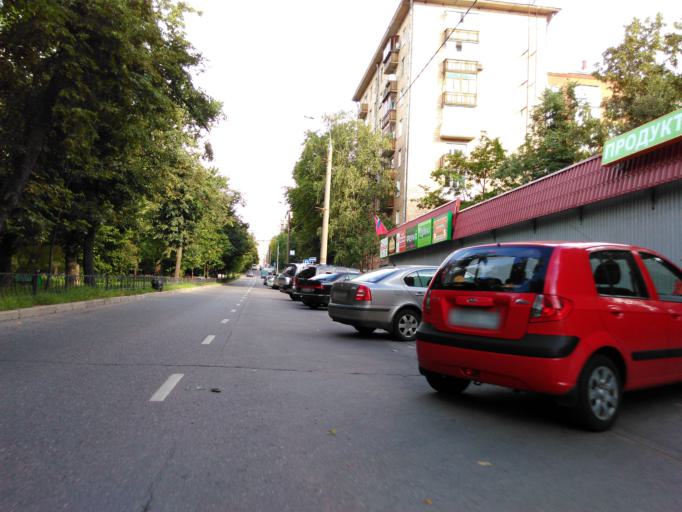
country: RU
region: Moskovskaya
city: Semenovskoye
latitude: 55.6838
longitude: 37.5268
